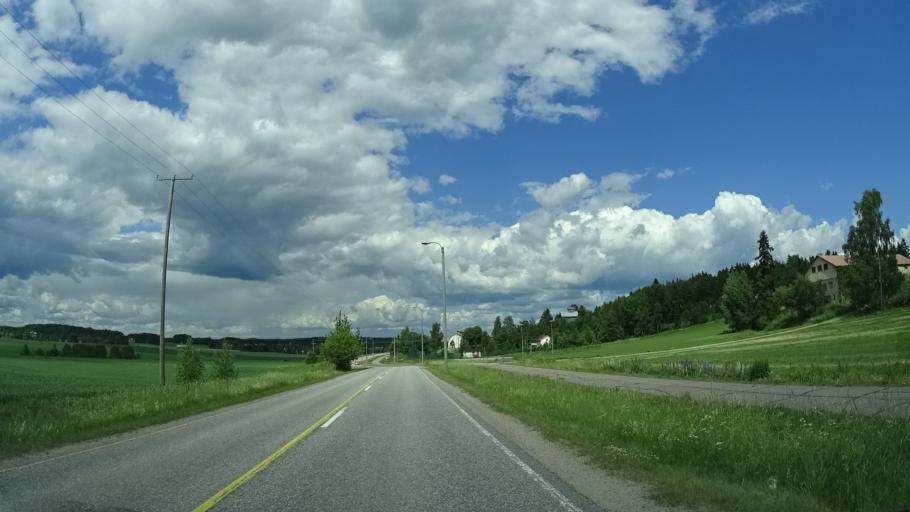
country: FI
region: Uusimaa
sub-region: Helsinki
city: Nurmijaervi
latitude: 60.3930
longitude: 24.6429
